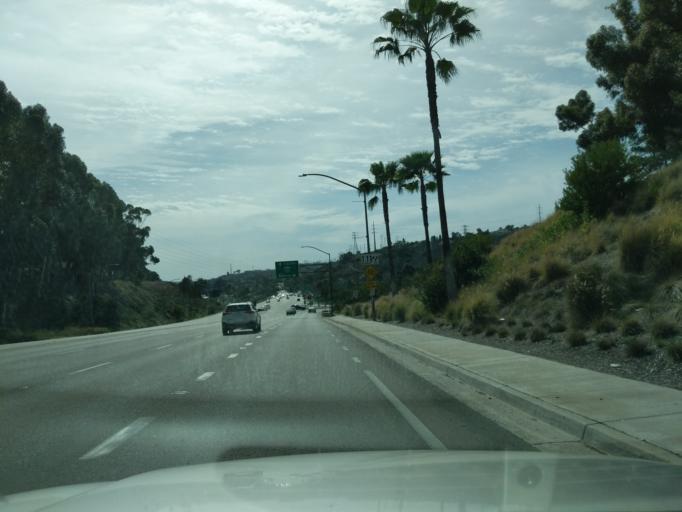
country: US
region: California
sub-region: San Diego County
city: San Diego
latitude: 32.7893
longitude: -117.1100
